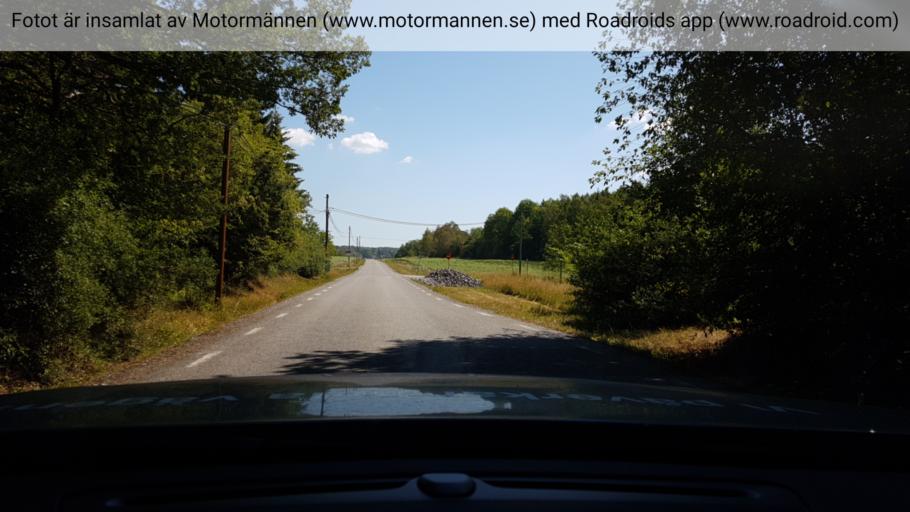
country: SE
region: Stockholm
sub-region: Upplands-Bro Kommun
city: Kungsaengen
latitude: 59.4068
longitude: 17.7179
